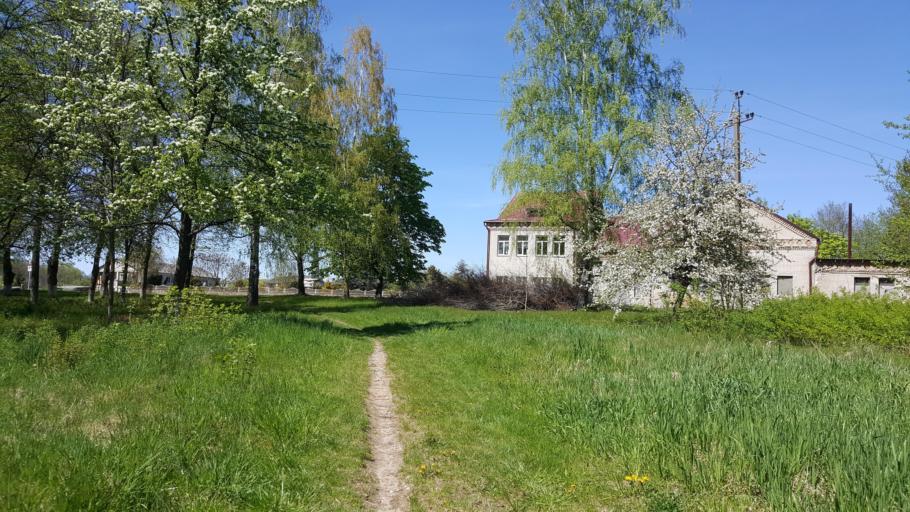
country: BY
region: Brest
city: Kamyanyets
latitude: 52.4400
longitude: 23.8474
